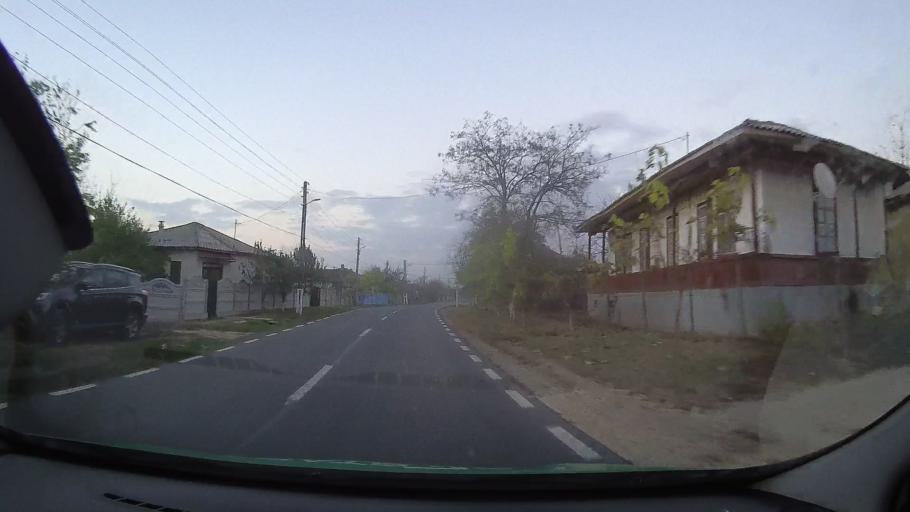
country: RO
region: Constanta
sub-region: Comuna Oltina
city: Oltina
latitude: 44.1649
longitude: 27.6672
